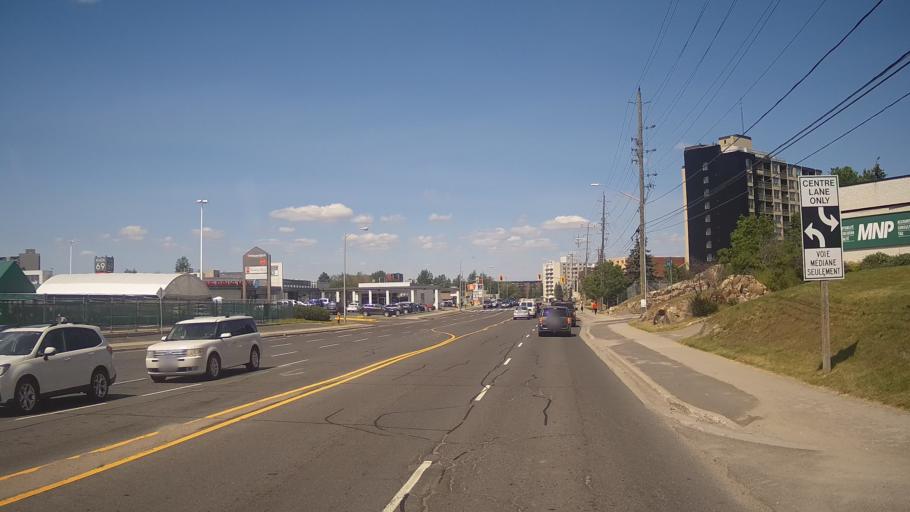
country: CA
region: Ontario
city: Greater Sudbury
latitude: 46.4518
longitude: -81.0027
